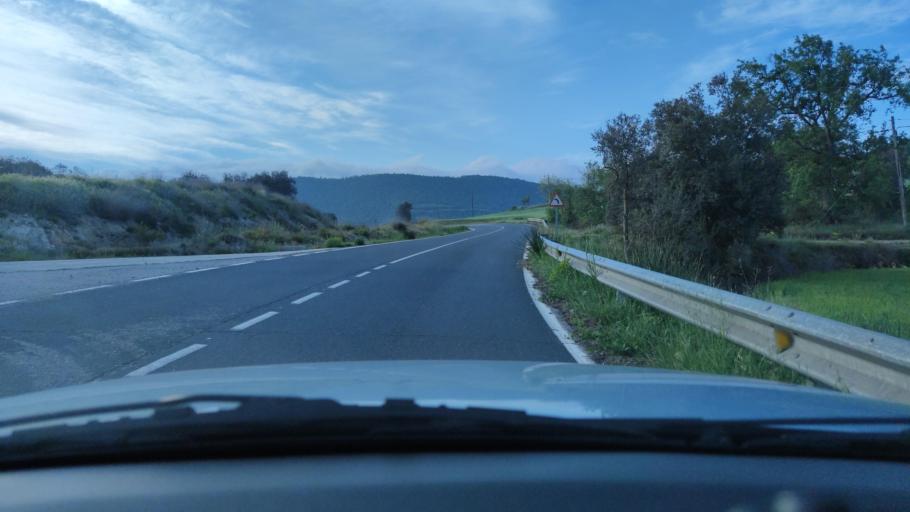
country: ES
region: Catalonia
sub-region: Provincia de Lleida
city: Ponts
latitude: 41.8922
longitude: 1.1790
